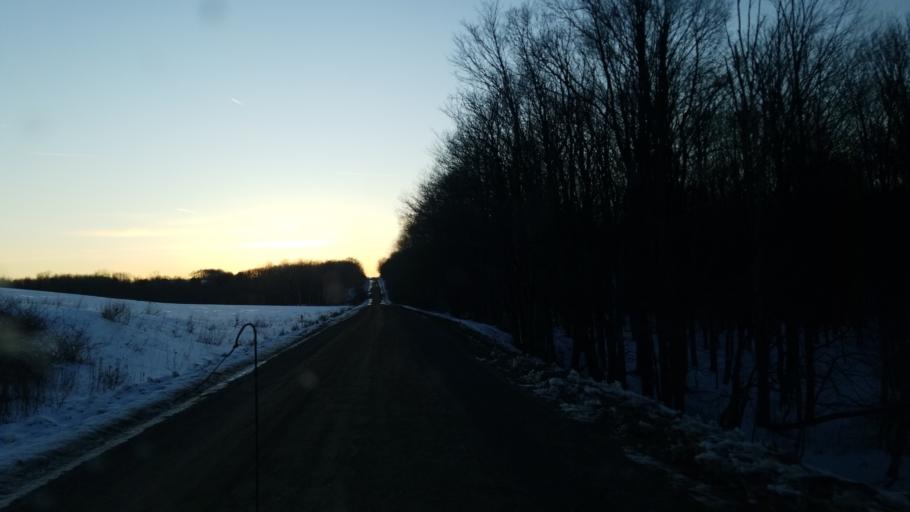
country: US
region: New York
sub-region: Allegany County
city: Andover
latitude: 42.0085
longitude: -77.7290
